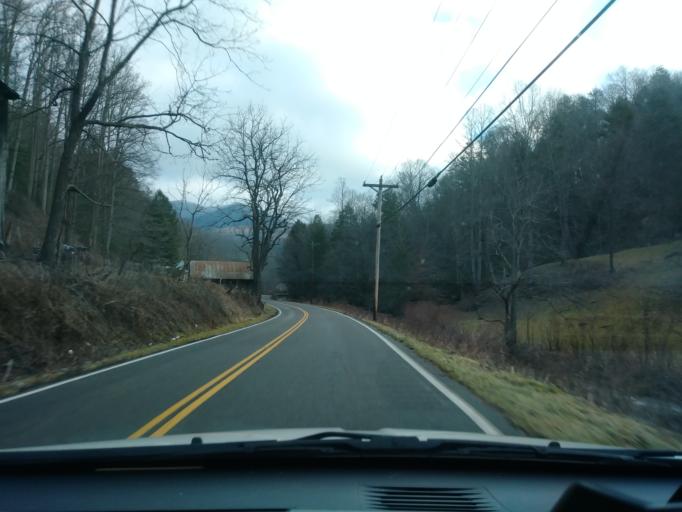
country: US
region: Tennessee
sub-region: Carter County
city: Elizabethton
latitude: 36.2233
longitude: -82.1946
